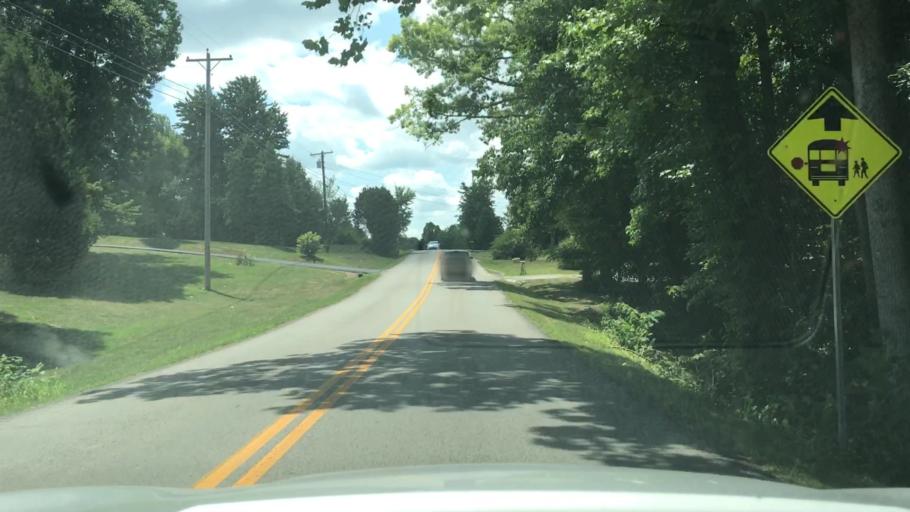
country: US
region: Kentucky
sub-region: Muhlenberg County
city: Greenville
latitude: 37.1949
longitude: -87.2133
